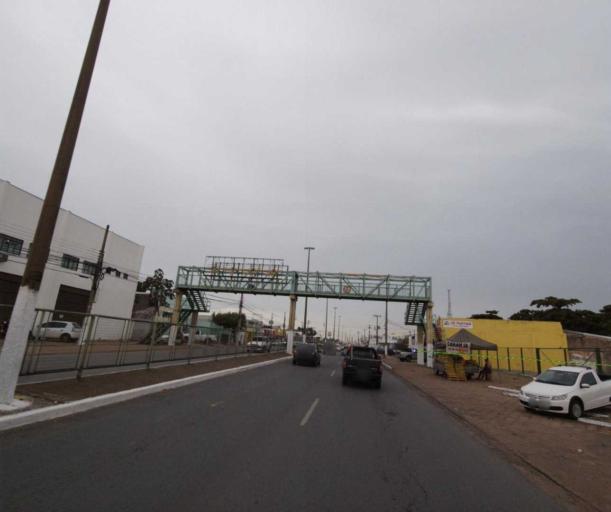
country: BR
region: Mato Grosso
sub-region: Cuiaba
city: Cuiaba
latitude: -15.6275
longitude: -56.0572
